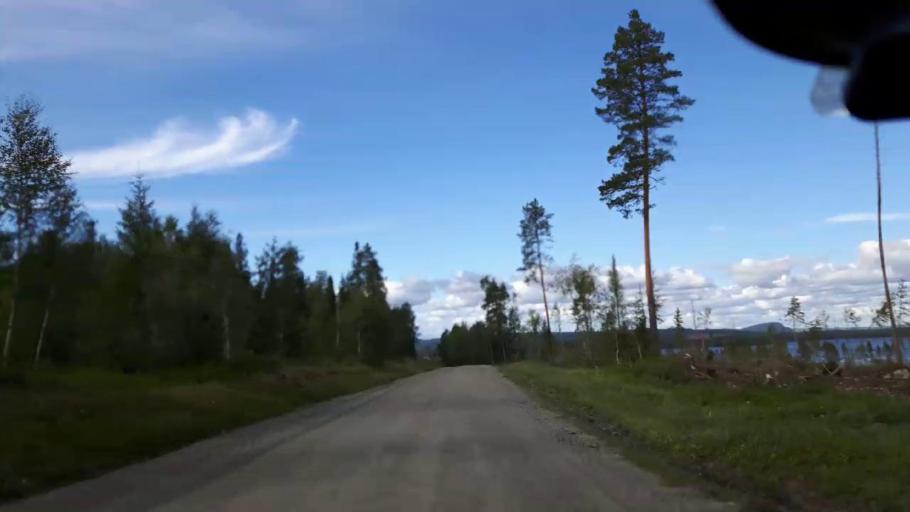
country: SE
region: Jaemtland
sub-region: Ragunda Kommun
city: Hammarstrand
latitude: 63.1357
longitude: 15.9459
